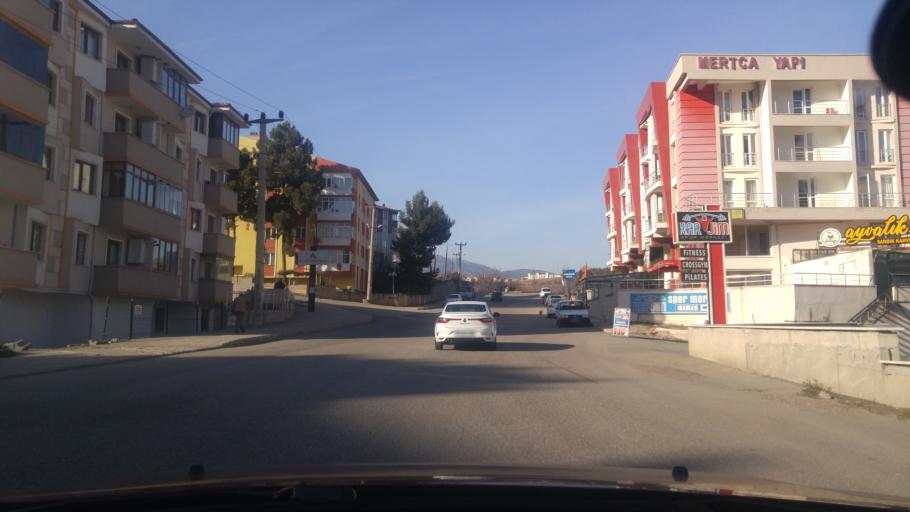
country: TR
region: Karabuk
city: Safranbolu
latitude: 41.2211
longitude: 32.6726
